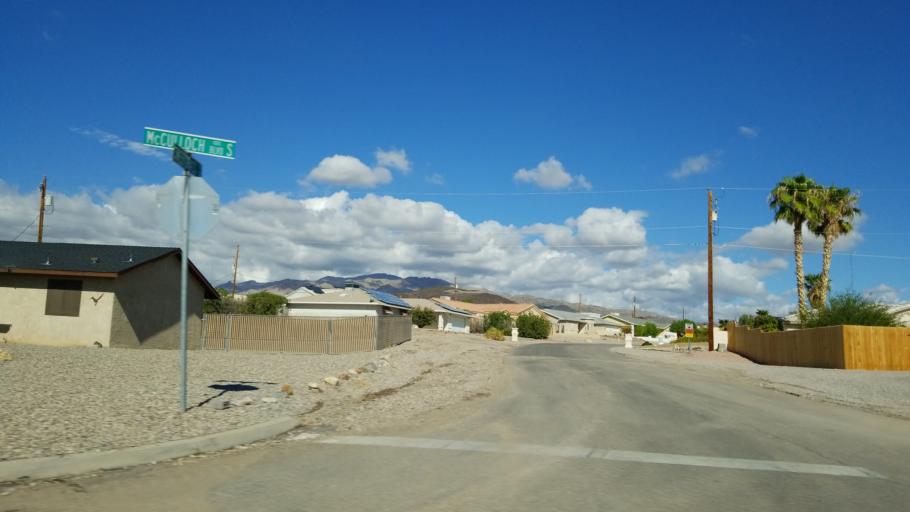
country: US
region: Arizona
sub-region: Mohave County
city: Lake Havasu City
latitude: 34.4756
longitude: -114.2662
